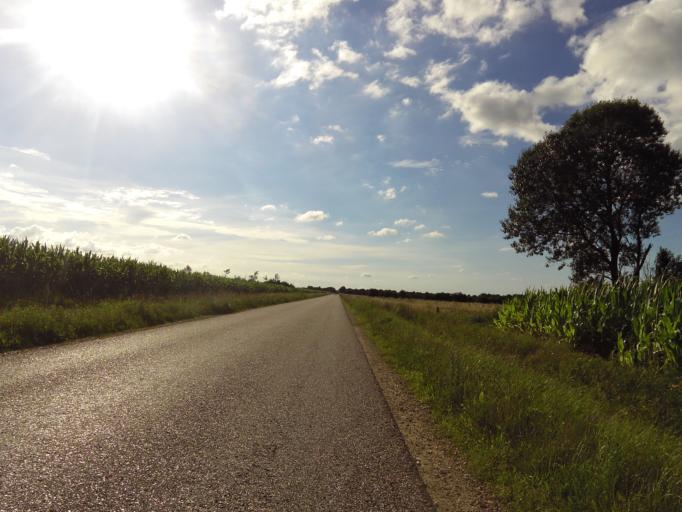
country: DK
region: South Denmark
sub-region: Haderslev Kommune
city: Vojens
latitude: 55.2008
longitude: 9.2928
